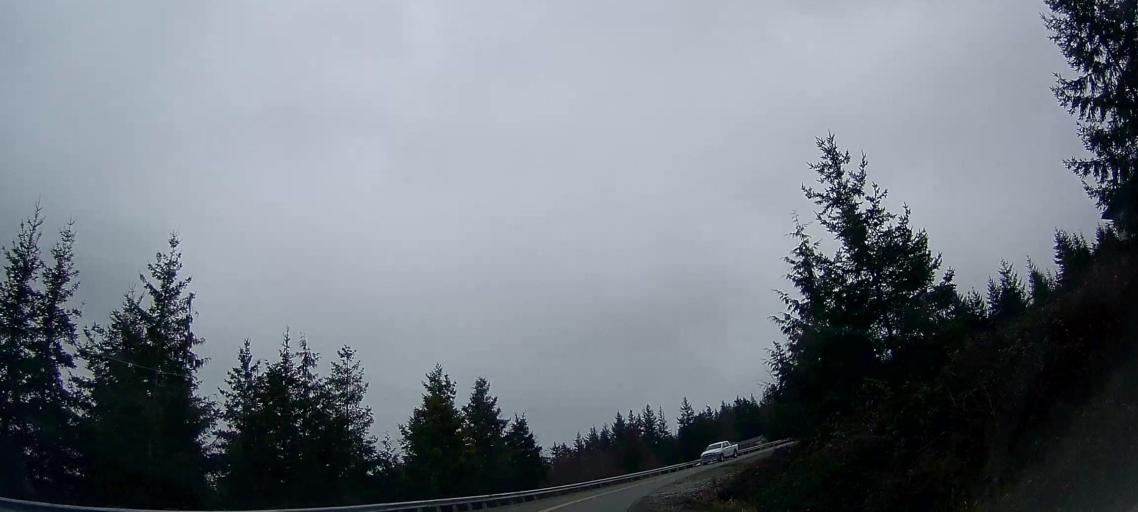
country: US
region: Washington
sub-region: Skagit County
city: Mount Vernon
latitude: 48.3784
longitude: -122.2987
